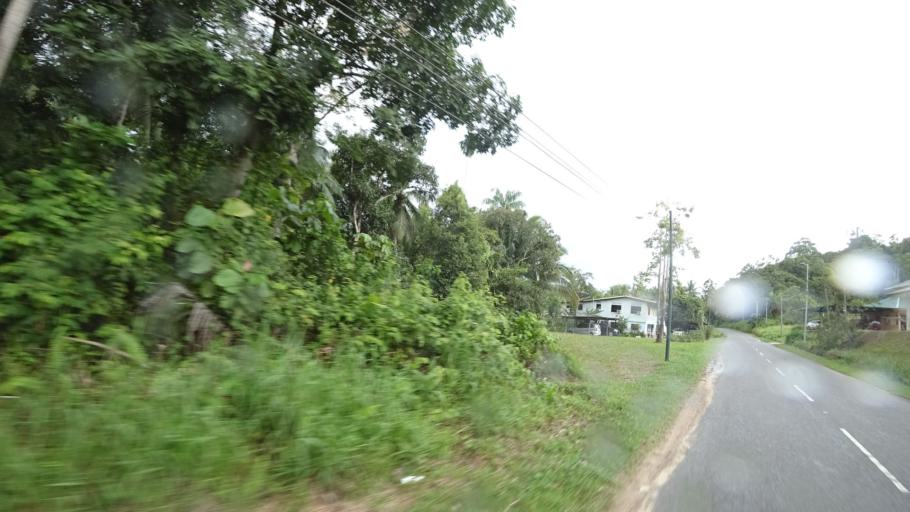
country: BN
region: Brunei and Muara
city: Bandar Seri Begawan
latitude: 4.8467
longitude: 114.9530
